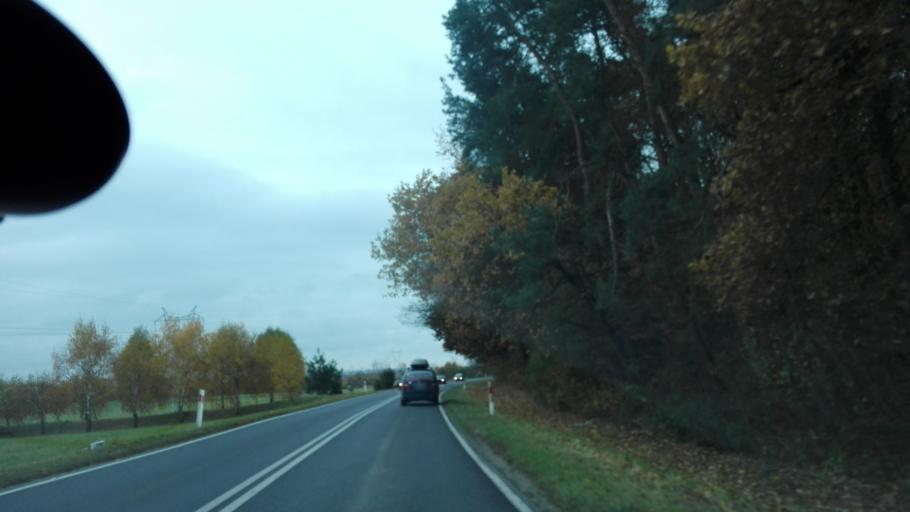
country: PL
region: Lublin Voivodeship
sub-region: Powiat pulawski
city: Pulawy
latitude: 51.4268
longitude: 21.9210
